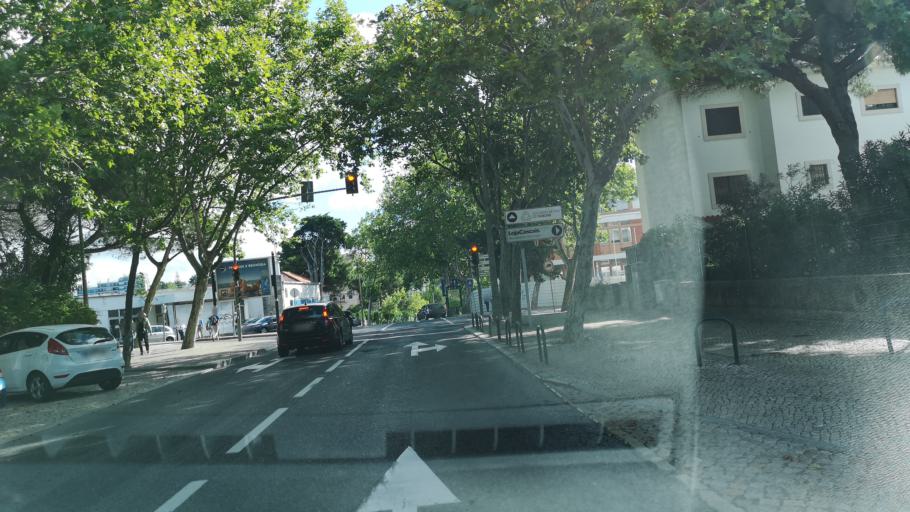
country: PT
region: Lisbon
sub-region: Cascais
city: Cascais
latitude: 38.7002
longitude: -9.4258
